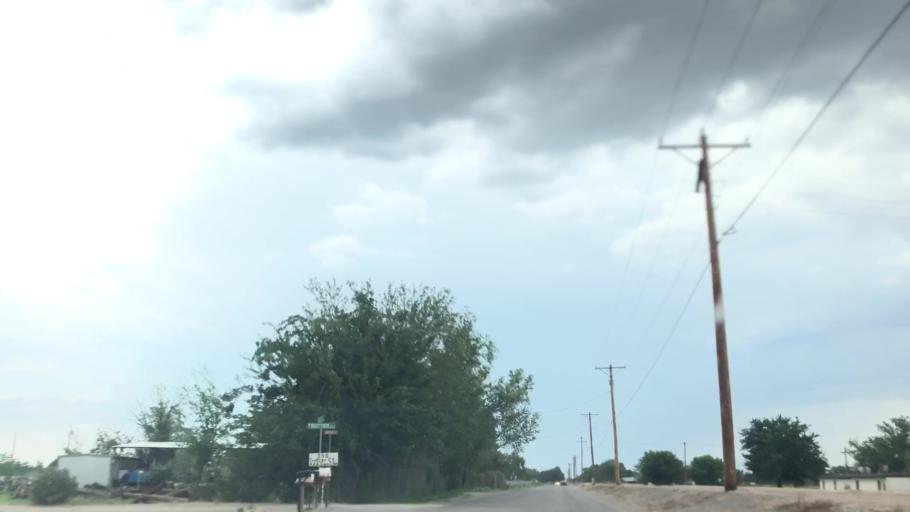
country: US
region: Texas
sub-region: El Paso County
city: Canutillo
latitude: 31.9130
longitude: -106.6249
